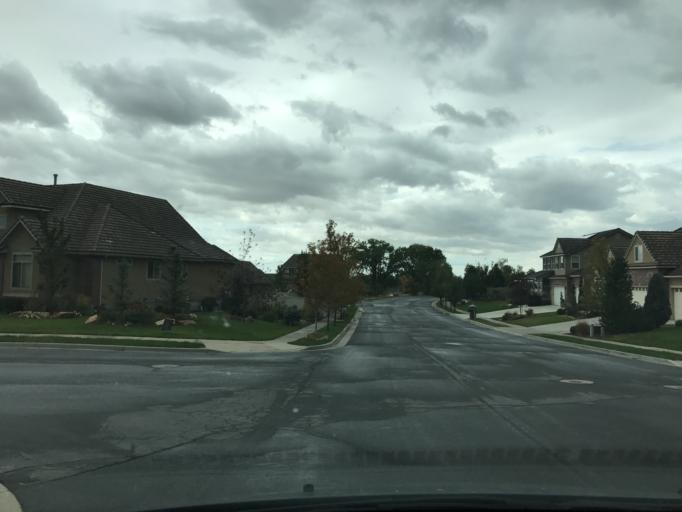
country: US
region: Utah
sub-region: Davis County
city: Fruit Heights
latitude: 41.0189
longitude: -111.9063
